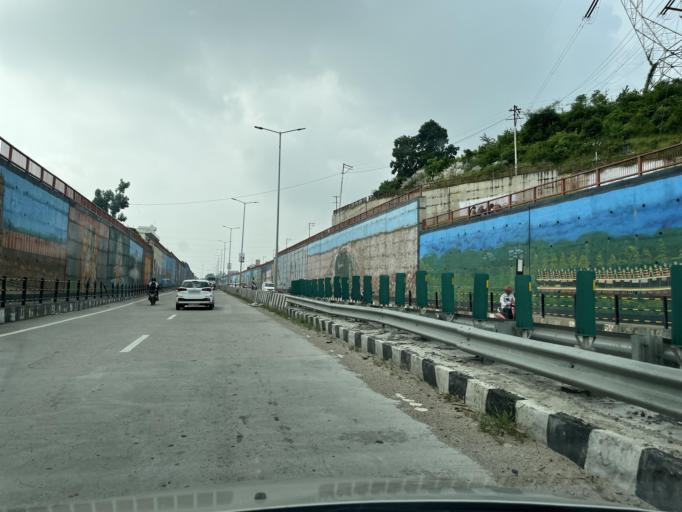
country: IN
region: Uttarakhand
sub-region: Dehradun
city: Raiwala
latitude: 30.0416
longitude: 78.2104
